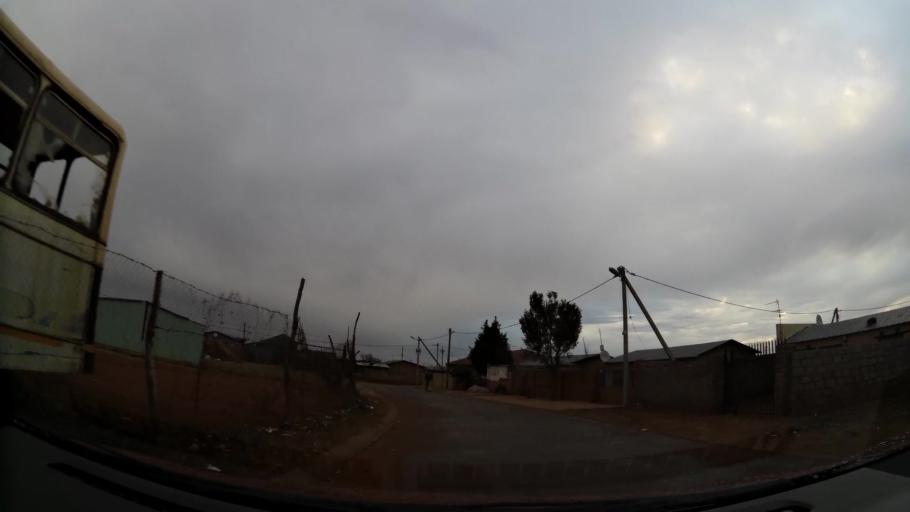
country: ZA
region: Gauteng
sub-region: West Rand District Municipality
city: Randfontein
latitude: -26.1726
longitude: 27.7866
